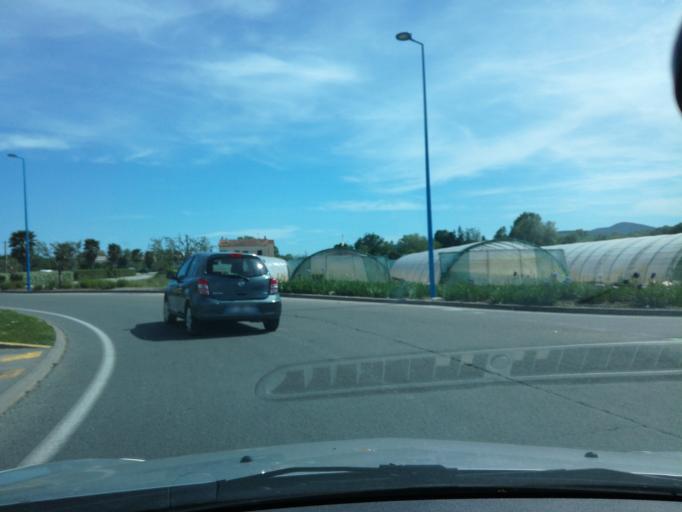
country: FR
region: Provence-Alpes-Cote d'Azur
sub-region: Departement des Alpes-Maritimes
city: Mandelieu-la-Napoule
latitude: 43.5669
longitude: 6.9482
